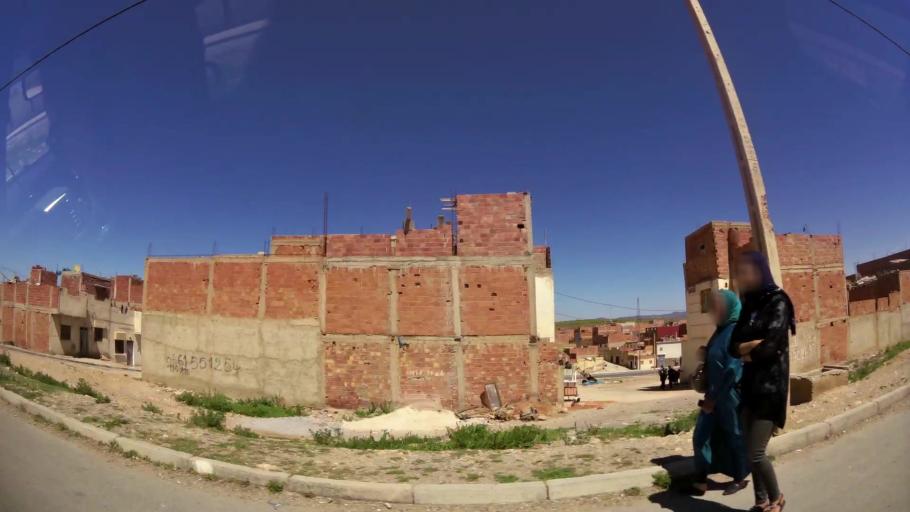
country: MA
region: Oriental
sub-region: Oujda-Angad
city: Oujda
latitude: 34.6548
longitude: -1.8672
